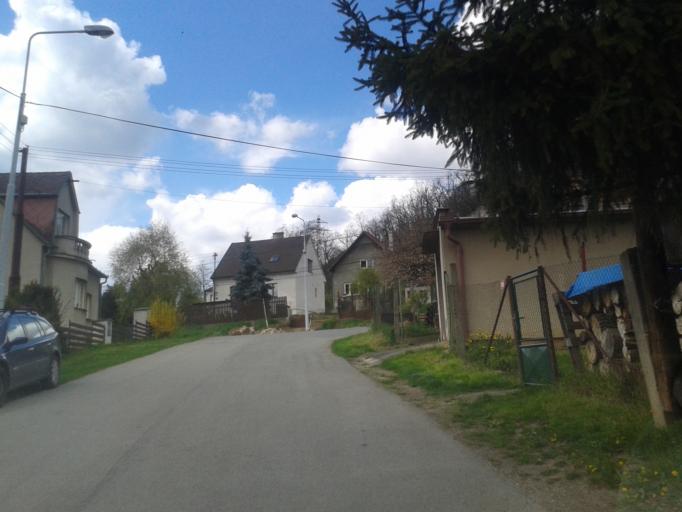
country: CZ
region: Central Bohemia
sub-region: Okres Beroun
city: Lodenice
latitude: 50.0011
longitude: 14.1600
